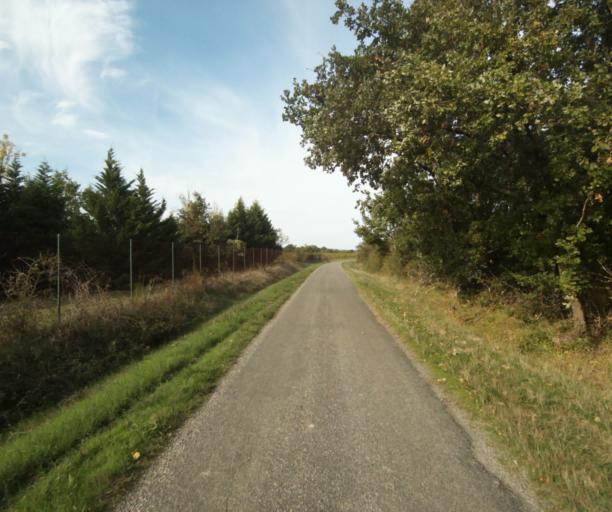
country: FR
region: Midi-Pyrenees
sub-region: Departement du Tarn-et-Garonne
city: Campsas
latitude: 43.9175
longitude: 1.3230
